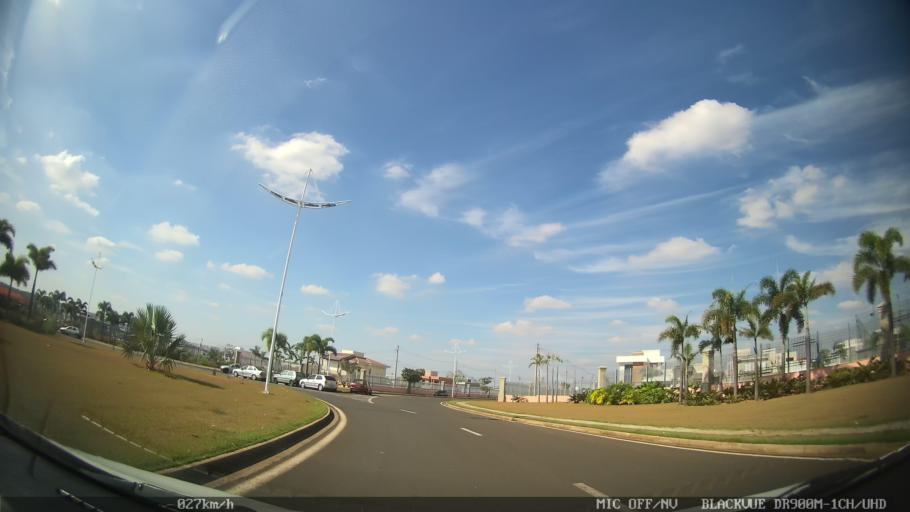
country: BR
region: Sao Paulo
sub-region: Hortolandia
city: Hortolandia
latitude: -22.8706
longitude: -47.2322
